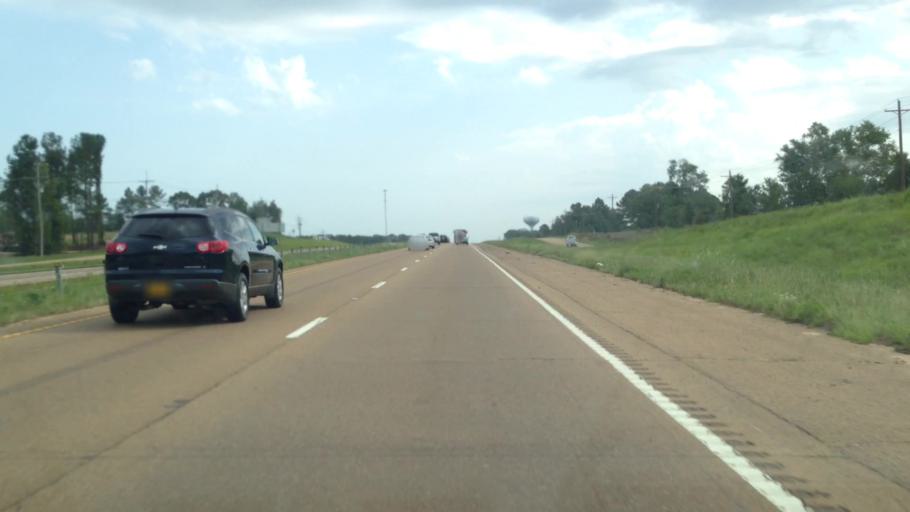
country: US
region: Mississippi
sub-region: Hinds County
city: Byram
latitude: 32.1465
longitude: -90.2795
